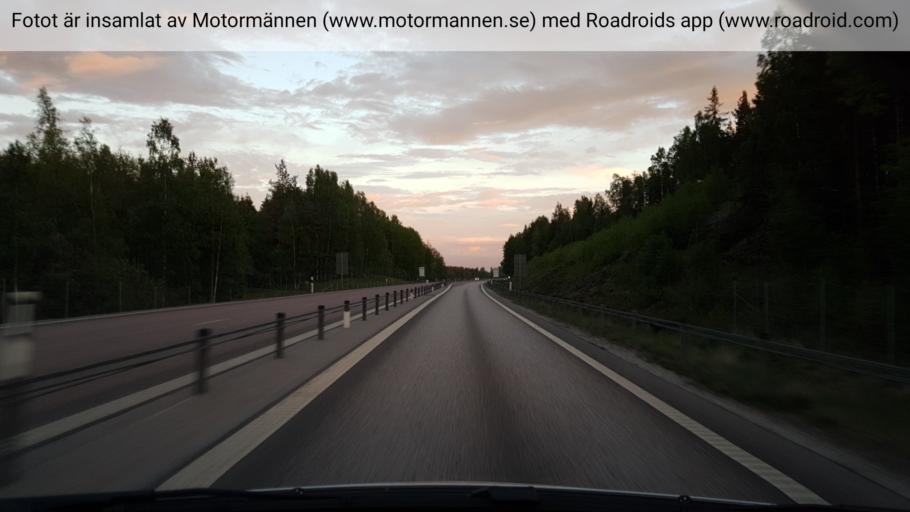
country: SE
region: Vaestmanland
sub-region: Surahammars Kommun
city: Ramnas
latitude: 59.7999
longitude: 16.1448
